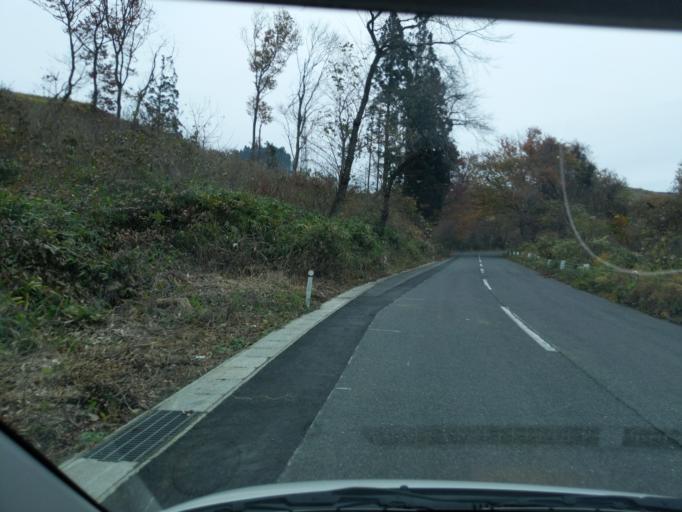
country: JP
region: Iwate
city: Mizusawa
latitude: 39.0409
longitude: 141.0710
